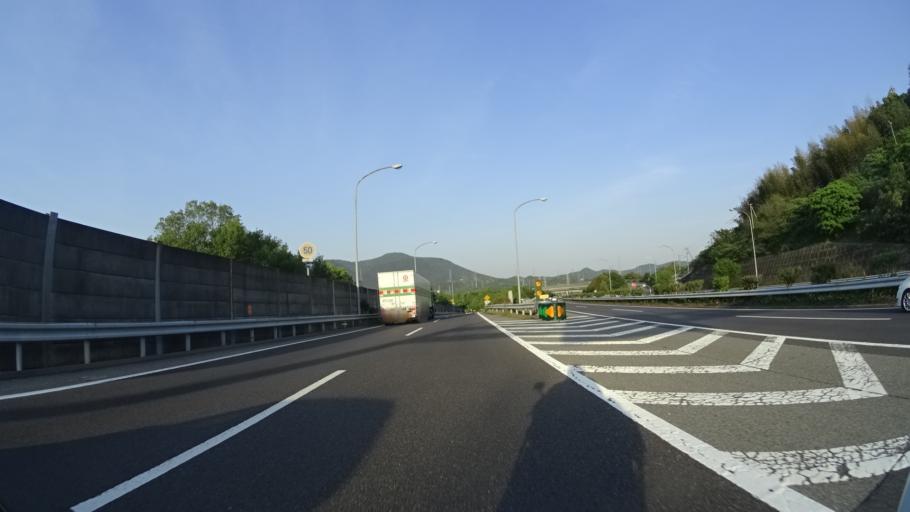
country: JP
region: Kagawa
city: Sakaidecho
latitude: 34.2821
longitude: 133.8473
